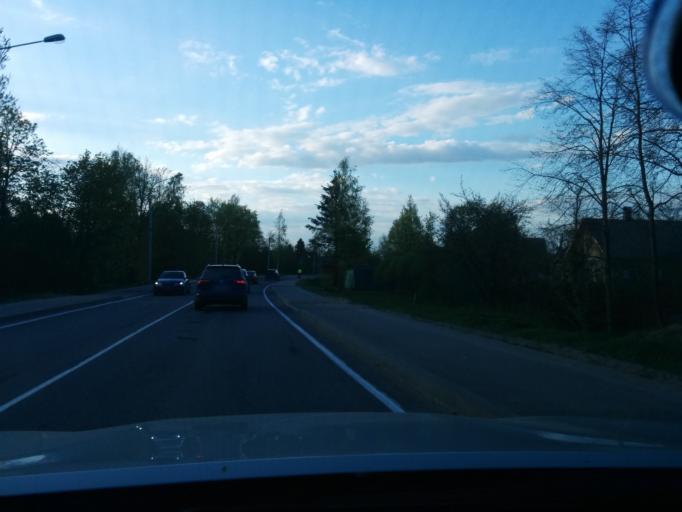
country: RU
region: Leningrad
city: Verkhniye Osel'ki
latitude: 60.2453
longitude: 30.4450
